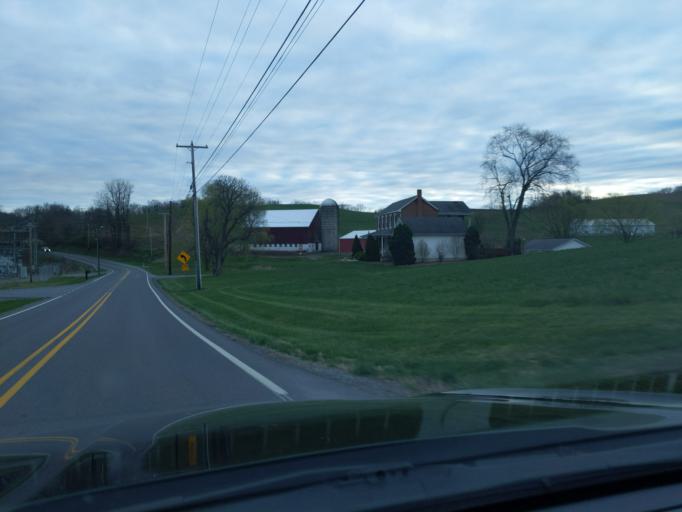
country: US
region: Pennsylvania
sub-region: Blair County
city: Lakemont
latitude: 40.4615
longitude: -78.3476
